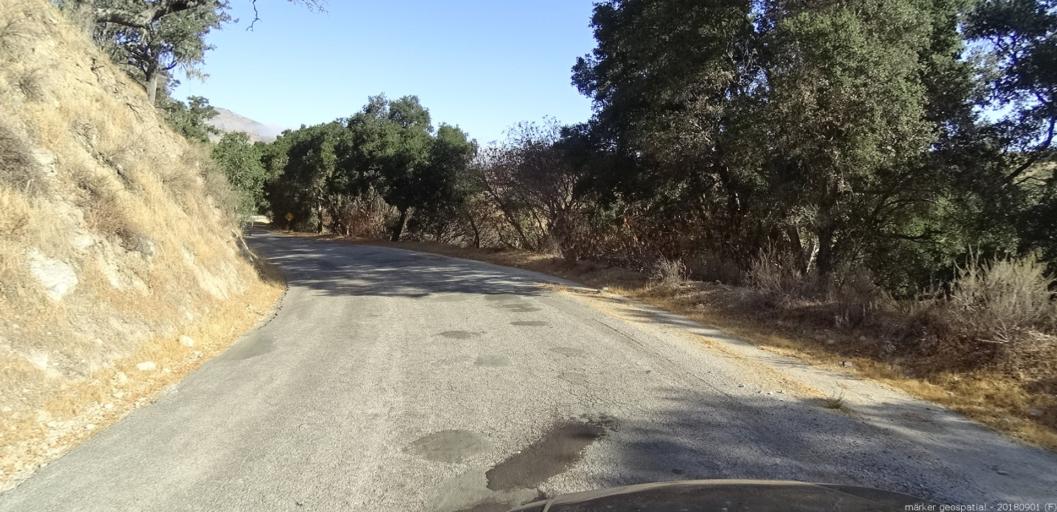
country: US
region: California
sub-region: Monterey County
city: Greenfield
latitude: 36.2367
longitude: -121.2844
